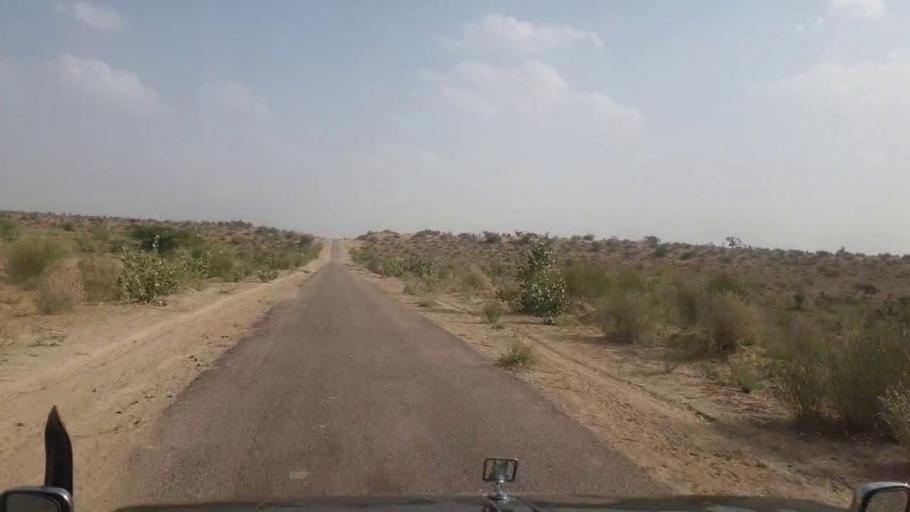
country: PK
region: Sindh
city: Islamkot
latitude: 25.1425
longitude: 70.3154
